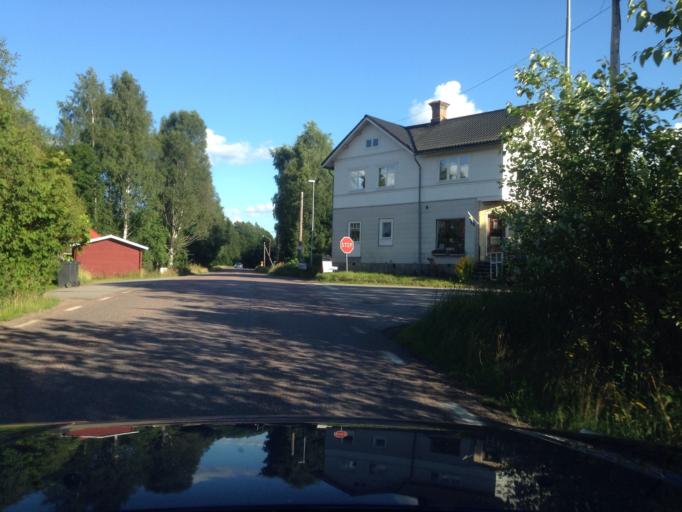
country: SE
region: Dalarna
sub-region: Ludvika Kommun
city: Grangesberg
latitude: 60.1449
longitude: 14.9884
